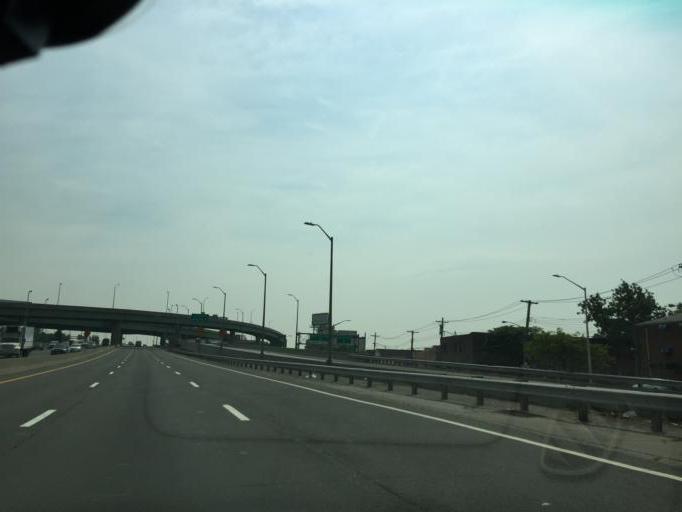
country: US
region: New York
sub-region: Bronx
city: The Bronx
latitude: 40.8275
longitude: -73.8480
